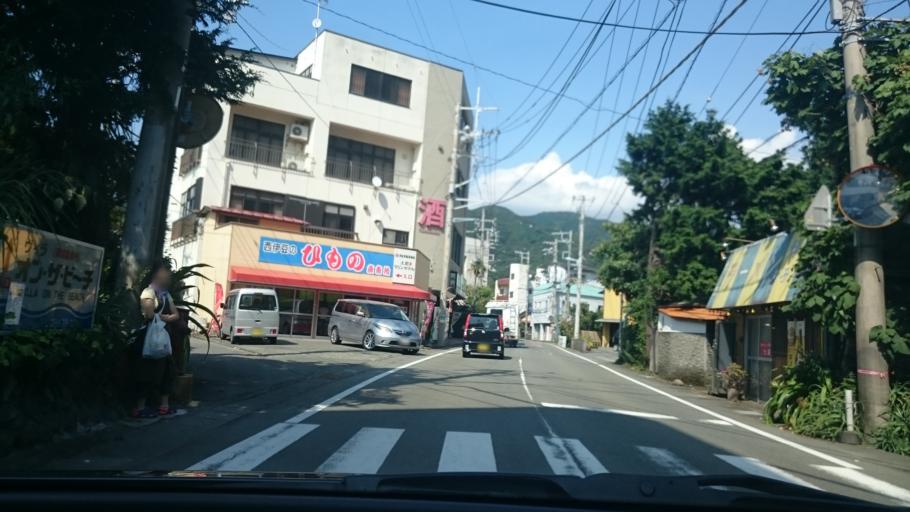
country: JP
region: Shizuoka
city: Heda
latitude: 34.9068
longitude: 138.7903
